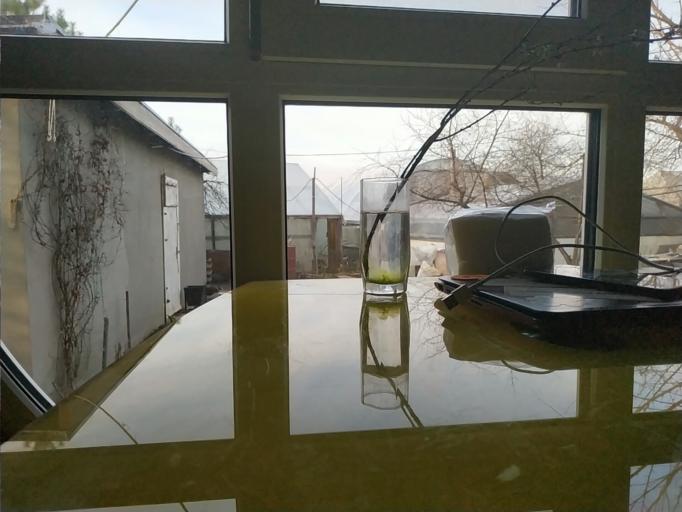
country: RU
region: Republic of Karelia
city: Suoyarvi
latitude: 62.0690
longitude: 32.1781
